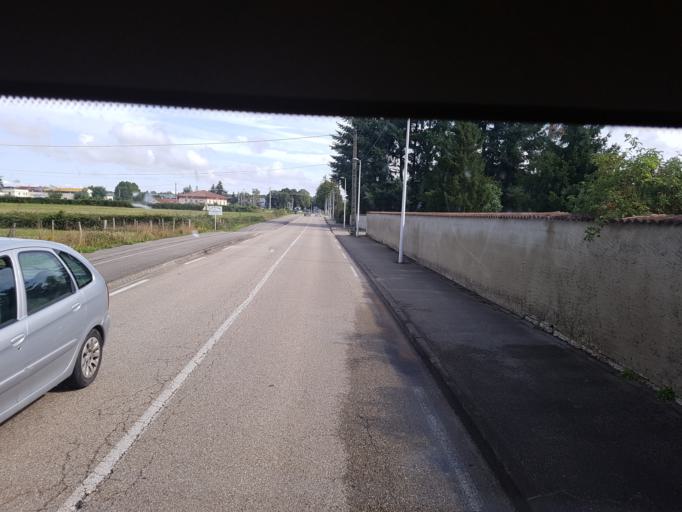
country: FR
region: Rhone-Alpes
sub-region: Departement de l'Ain
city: Bourg-en-Bresse
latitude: 46.1948
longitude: 5.2608
